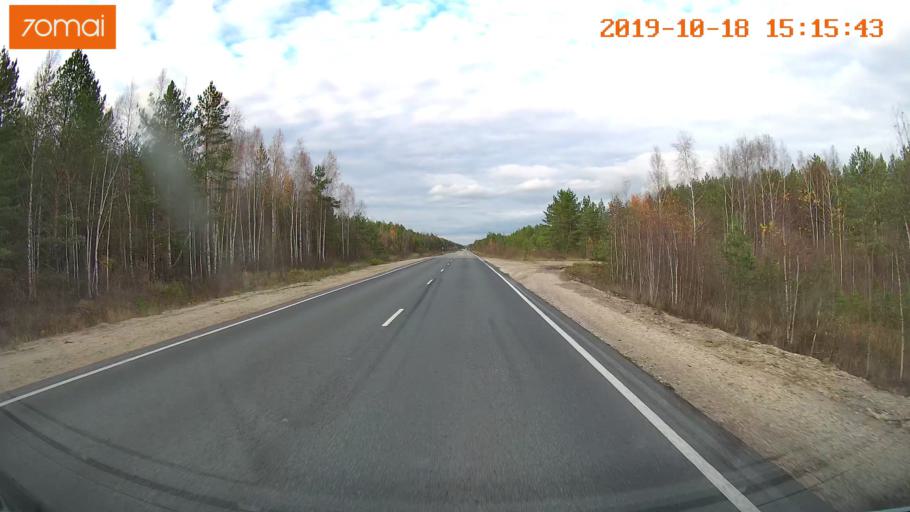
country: RU
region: Vladimir
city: Gus'-Khrustal'nyy
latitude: 55.6238
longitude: 40.7231
